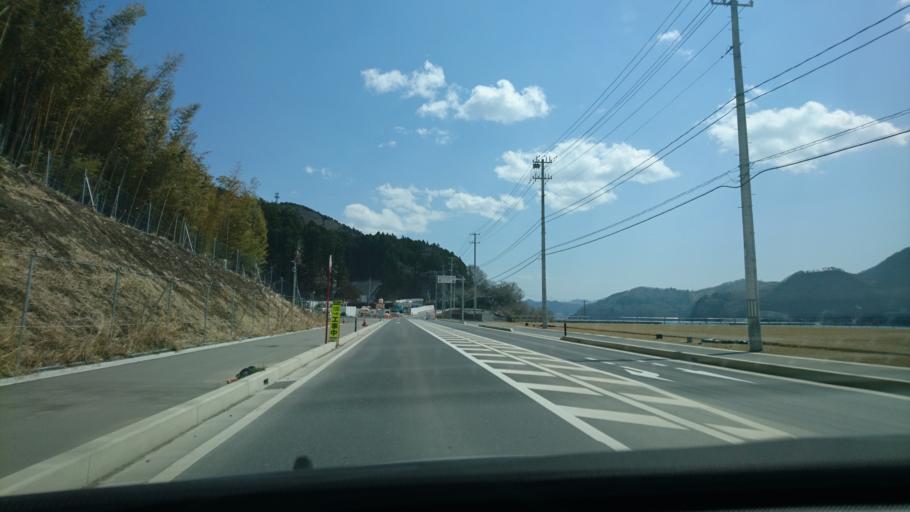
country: JP
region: Miyagi
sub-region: Oshika Gun
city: Onagawa Cho
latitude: 38.4462
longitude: 141.4615
